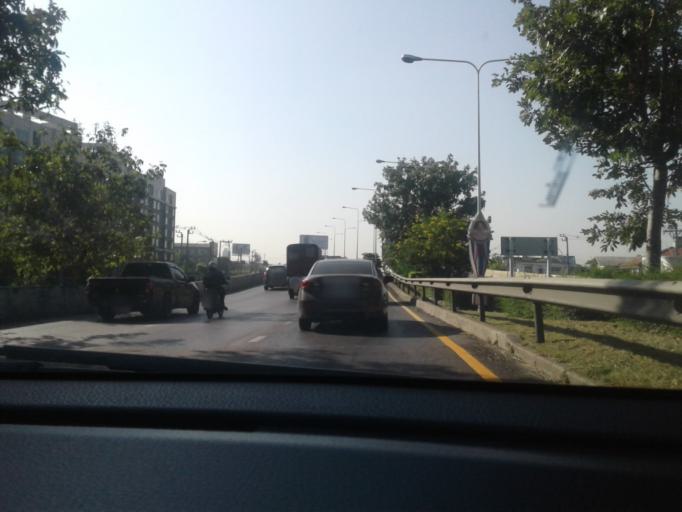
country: TH
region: Bangkok
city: Phasi Charoen
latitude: 13.7401
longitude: 100.4472
